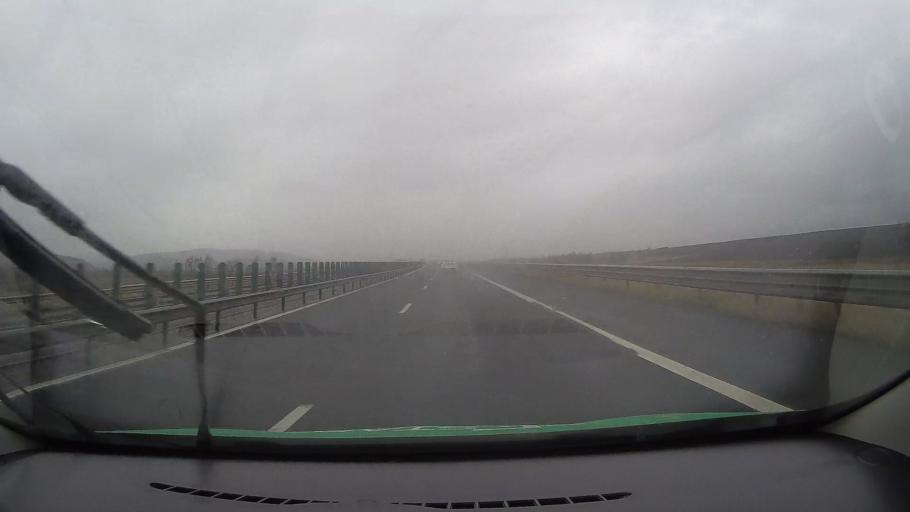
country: RO
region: Sibiu
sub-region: Oras Miercurea Sibiului
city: Miercurea Sibiului
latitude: 45.9000
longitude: 23.7640
